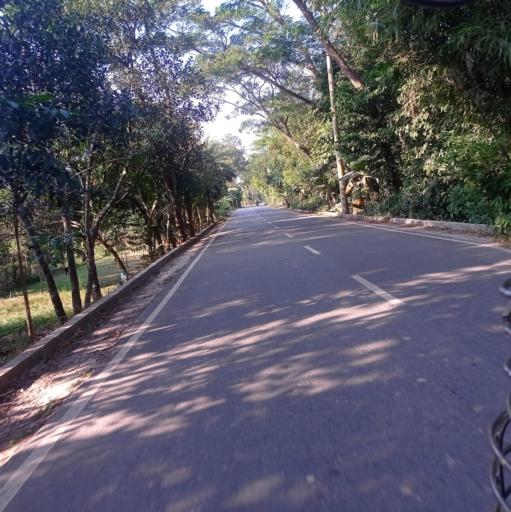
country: BD
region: Dhaka
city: Bajitpur
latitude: 24.1446
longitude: 90.8156
